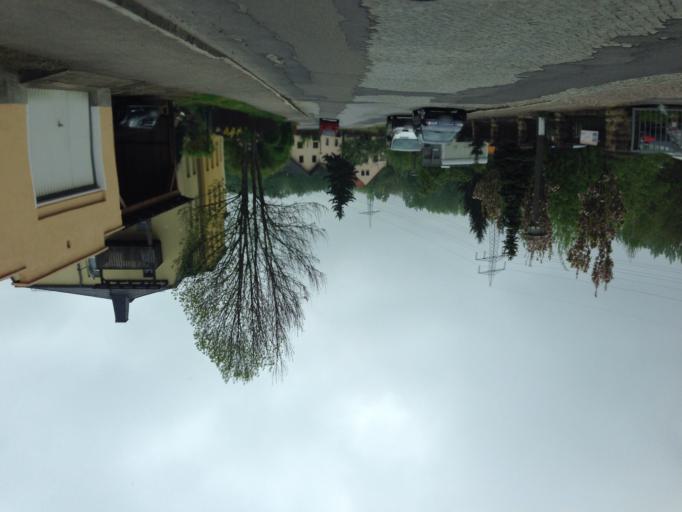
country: DE
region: Saxony
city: Freital
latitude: 51.0150
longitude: 13.6822
